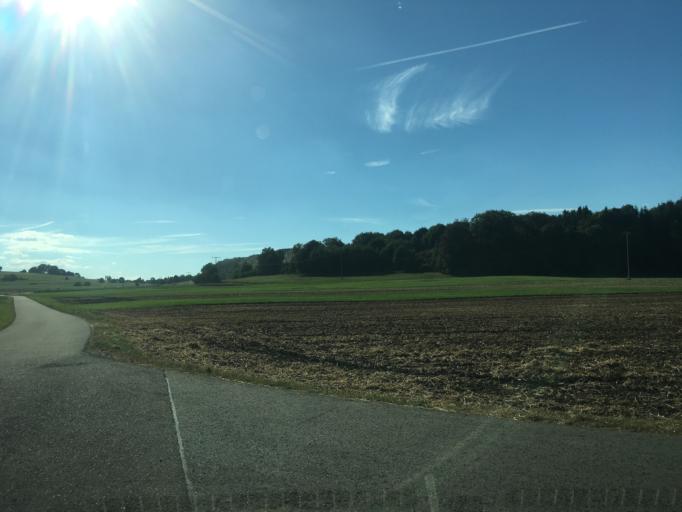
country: DE
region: Baden-Wuerttemberg
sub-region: Tuebingen Region
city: Pfullingen
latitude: 48.4134
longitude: 9.2119
